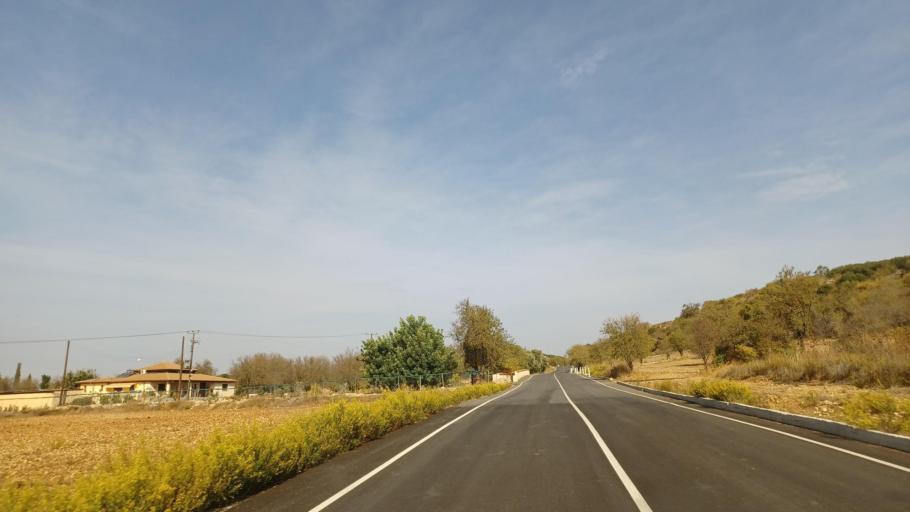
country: CY
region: Pafos
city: Polis
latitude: 34.9785
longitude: 32.5006
